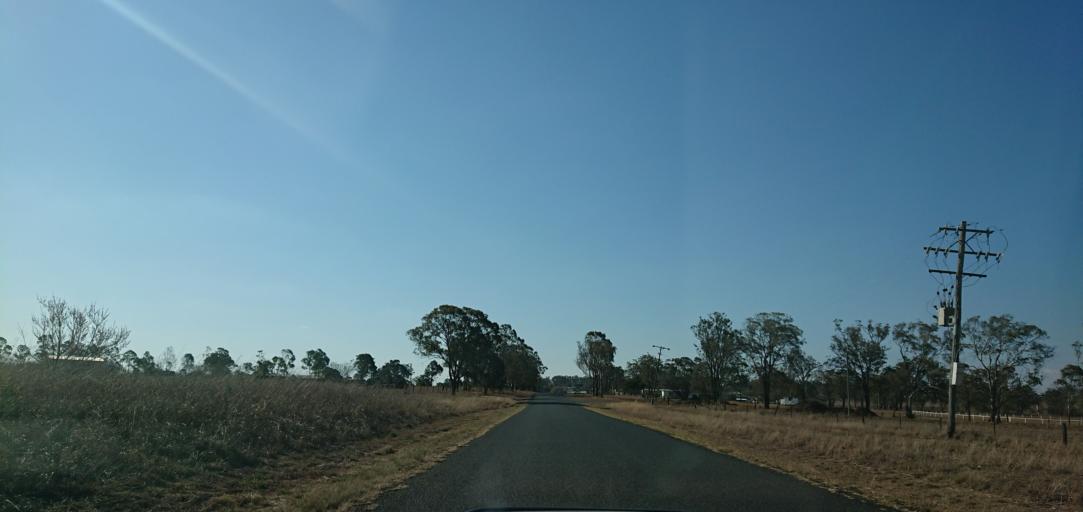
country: AU
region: Queensland
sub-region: Toowoomba
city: Westbrook
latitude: -27.6873
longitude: 151.7143
